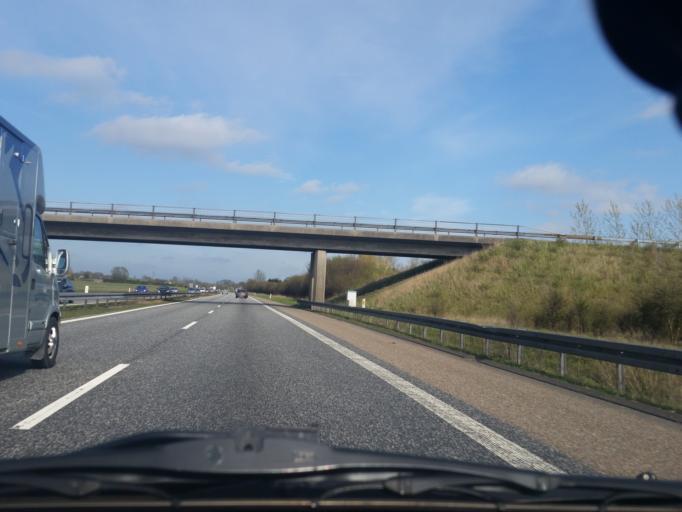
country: DK
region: Zealand
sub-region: Ringsted Kommune
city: Ringsted
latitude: 55.4481
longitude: 11.6820
